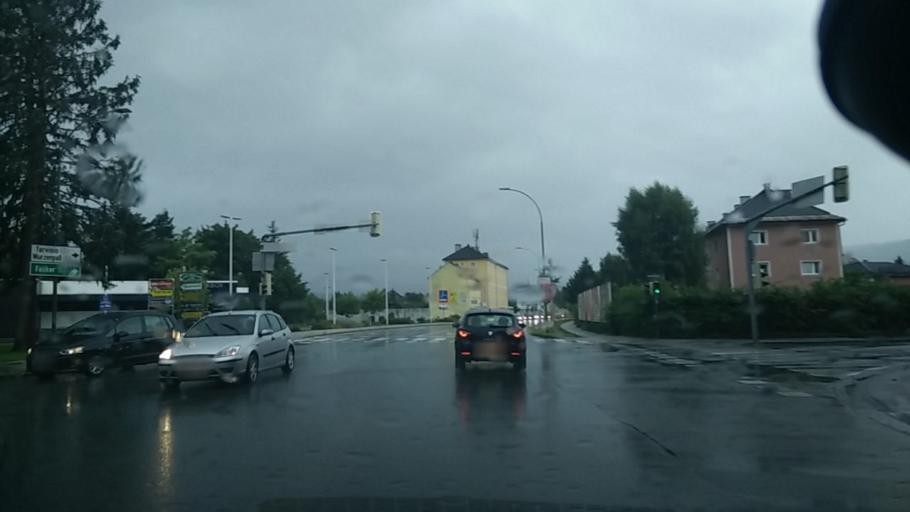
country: AT
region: Carinthia
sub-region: Villach Stadt
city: Villach
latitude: 46.6150
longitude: 13.8589
